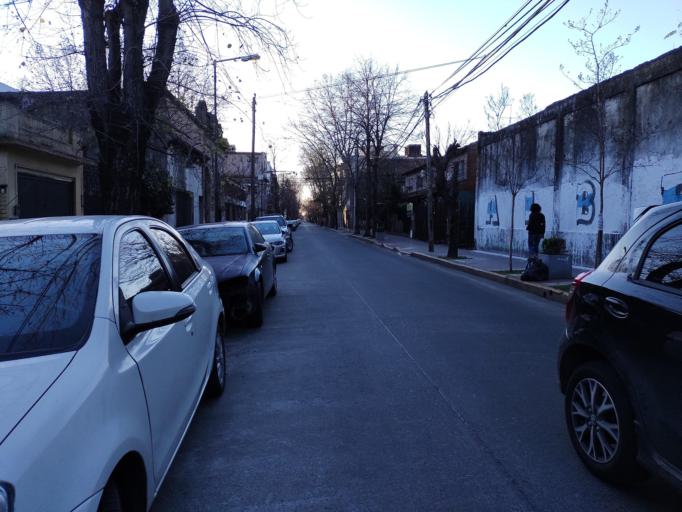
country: AR
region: Buenos Aires
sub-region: Partido de Tigre
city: Tigre
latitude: -34.4416
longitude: -58.5606
